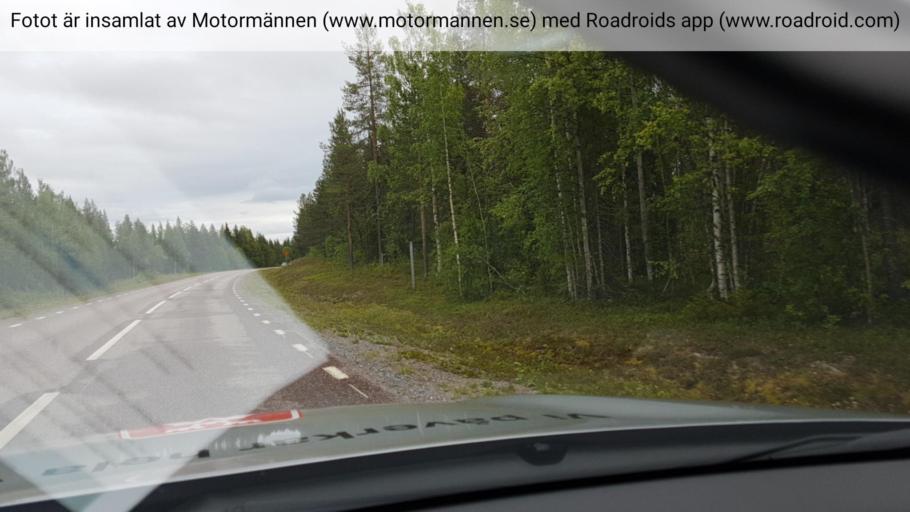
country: SE
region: Norrbotten
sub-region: Gallivare Kommun
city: Gaellivare
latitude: 67.0682
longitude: 21.5586
